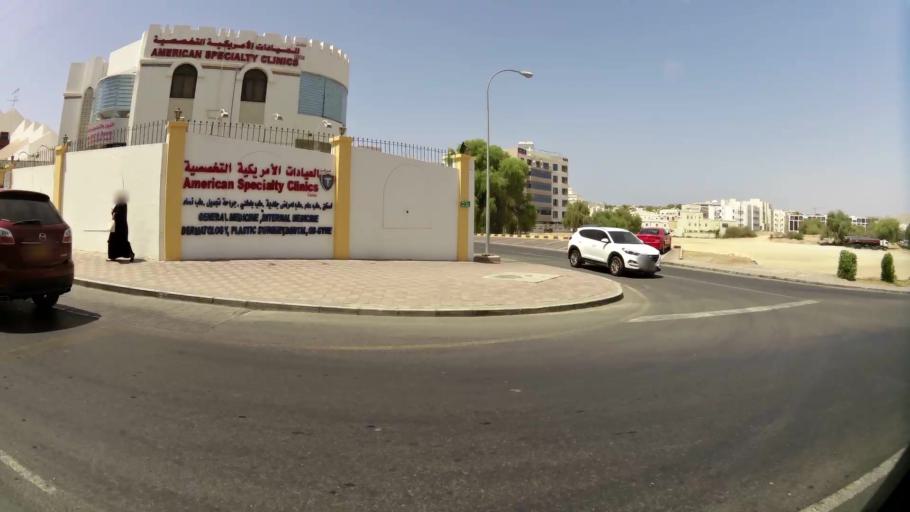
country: OM
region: Muhafazat Masqat
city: Muscat
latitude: 23.6231
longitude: 58.4874
